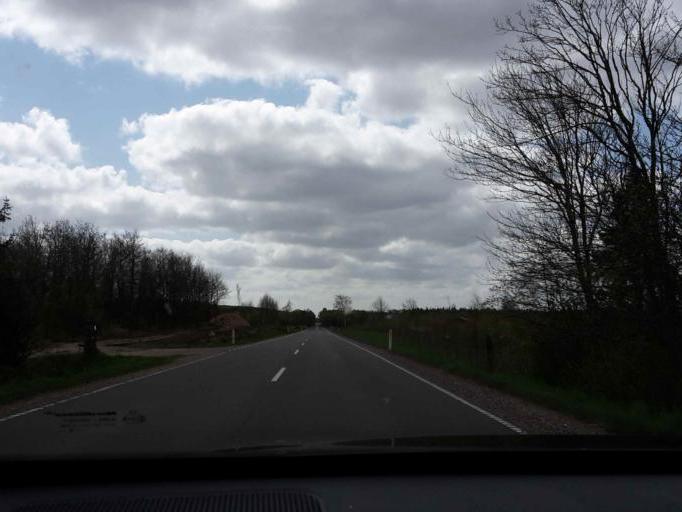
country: DK
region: South Denmark
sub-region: Varde Kommune
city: Olgod
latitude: 55.7058
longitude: 8.6076
